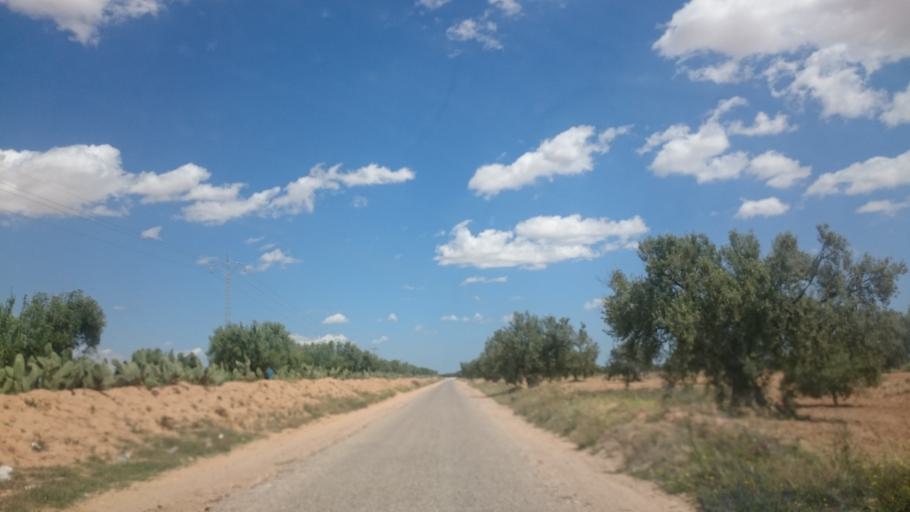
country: TN
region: Safaqis
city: Sfax
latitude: 34.6963
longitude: 10.5830
